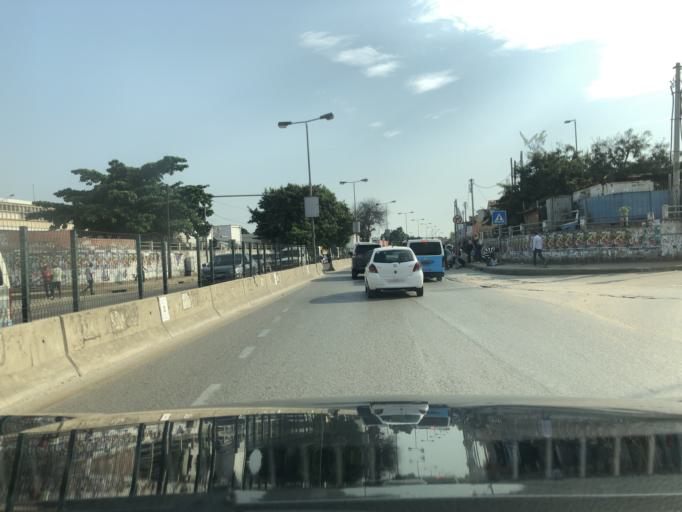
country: AO
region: Luanda
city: Luanda
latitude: -8.8434
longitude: 13.2399
